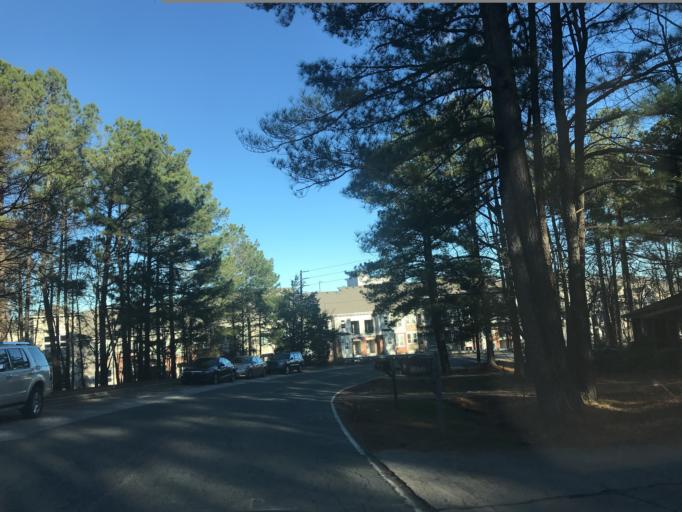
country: US
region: North Carolina
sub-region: Wake County
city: West Raleigh
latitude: 35.8393
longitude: -78.6851
